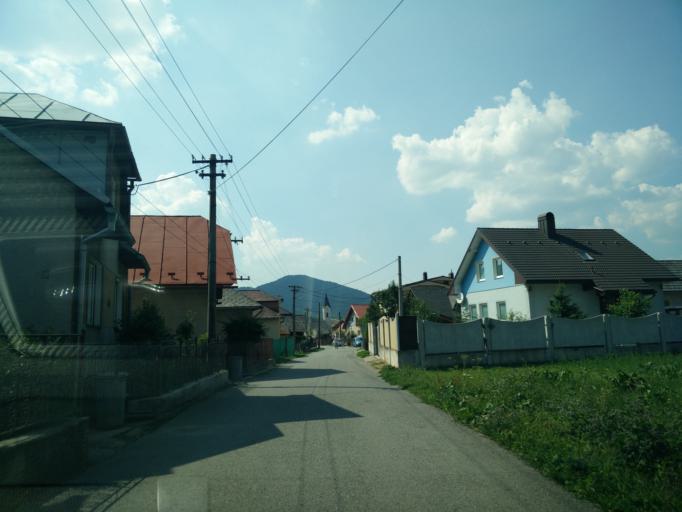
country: SK
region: Zilinsky
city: Rajec
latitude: 49.0428
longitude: 18.6397
